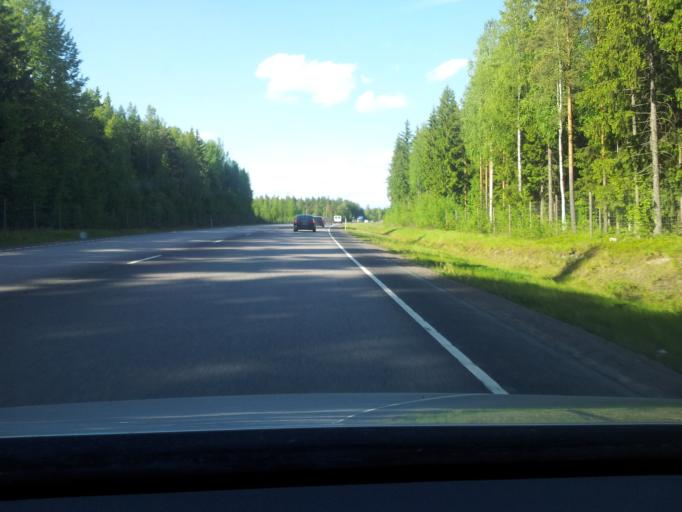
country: FI
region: Uusimaa
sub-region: Loviisa
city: Lapinjaervi
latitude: 60.6789
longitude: 26.2570
